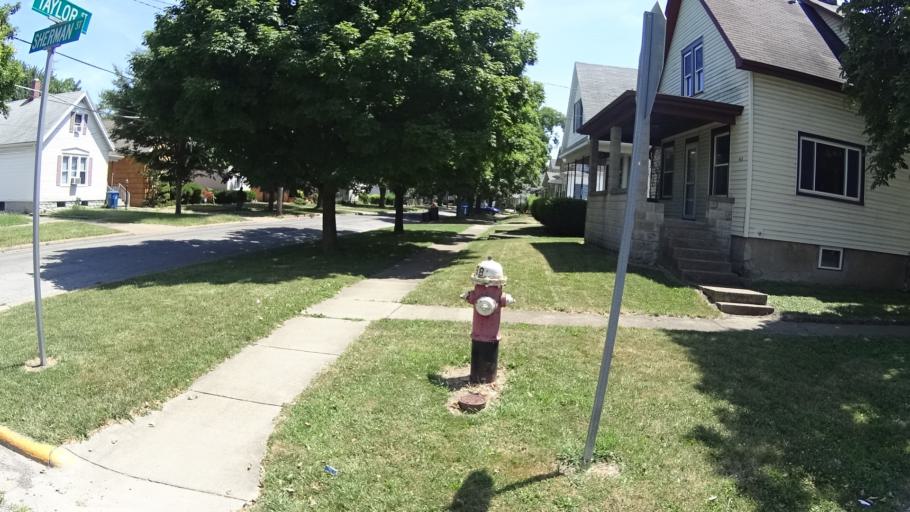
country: US
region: Ohio
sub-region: Erie County
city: Sandusky
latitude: 41.4411
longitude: -82.7076
